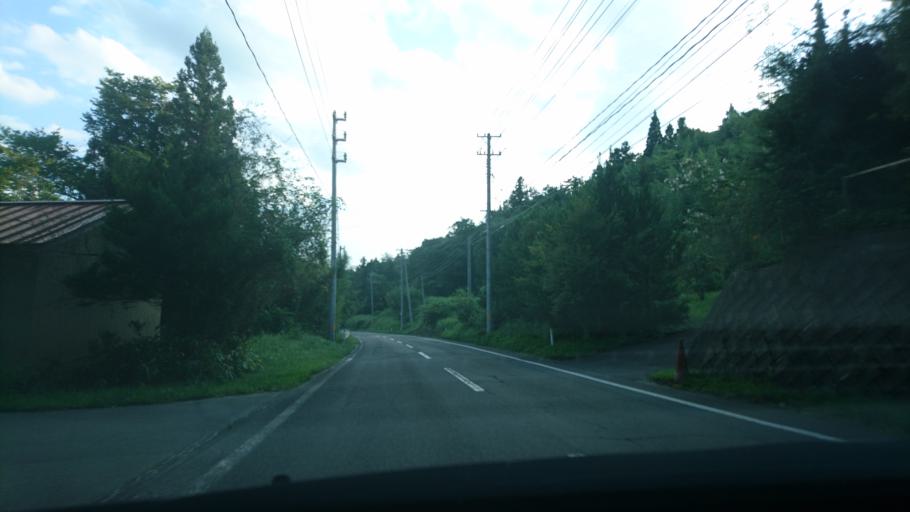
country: JP
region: Iwate
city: Ichinoseki
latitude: 39.0081
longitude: 141.2853
